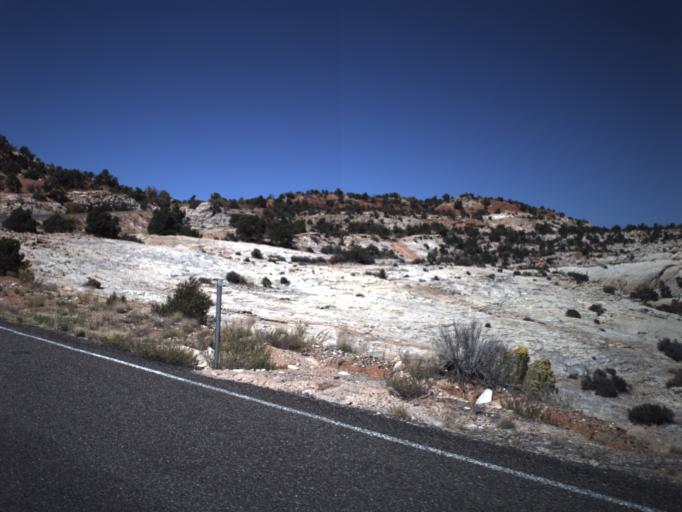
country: US
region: Utah
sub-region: Wayne County
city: Loa
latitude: 37.7475
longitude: -111.4552
